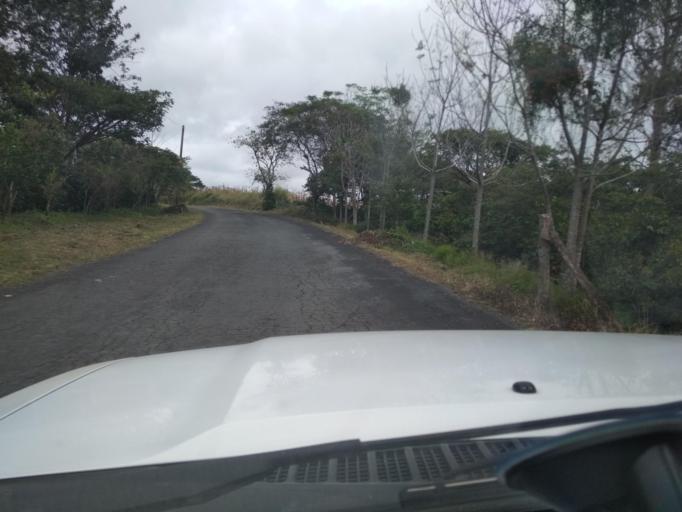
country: MX
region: Veracruz
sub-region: Emiliano Zapata
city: Dos Rios
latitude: 19.5335
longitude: -96.8084
